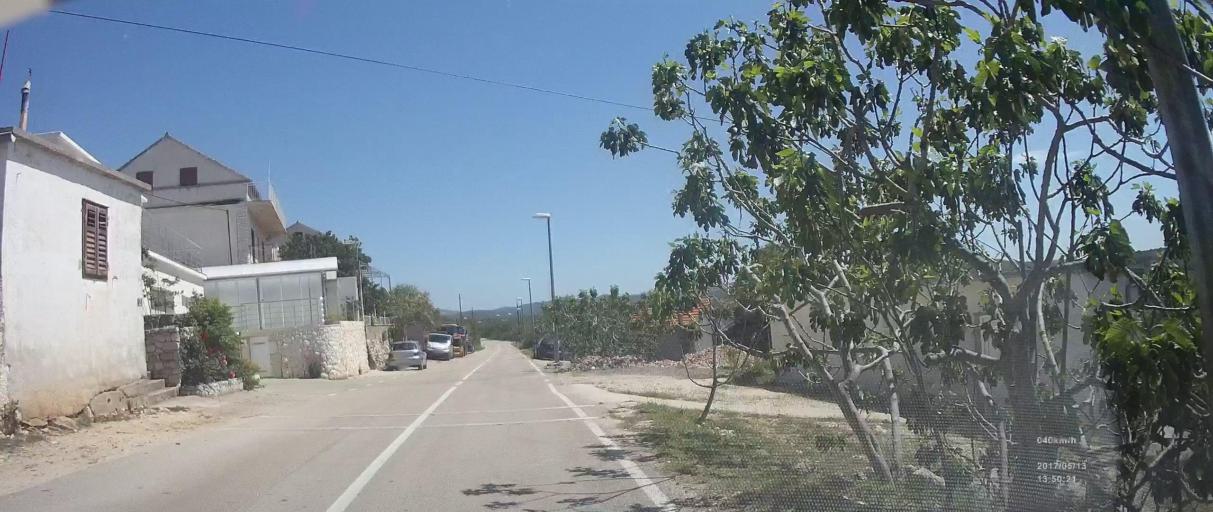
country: HR
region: Sibensko-Kniniska
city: Primosten
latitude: 43.6111
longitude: 15.9823
